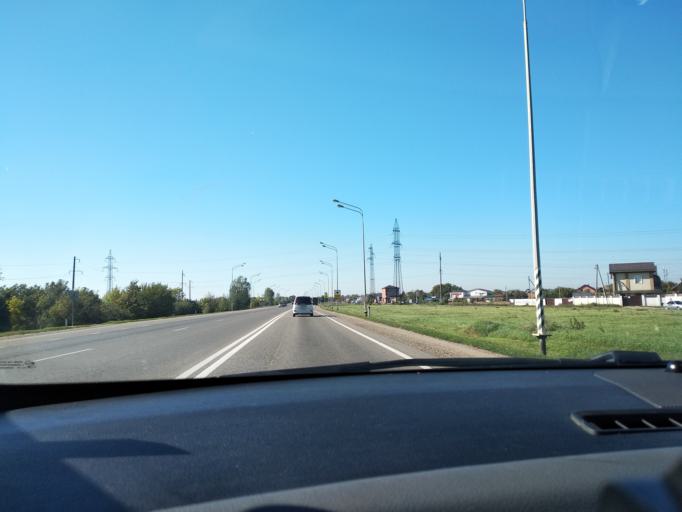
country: RU
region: Krasnodarskiy
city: Agronom
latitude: 45.1604
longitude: 39.0791
